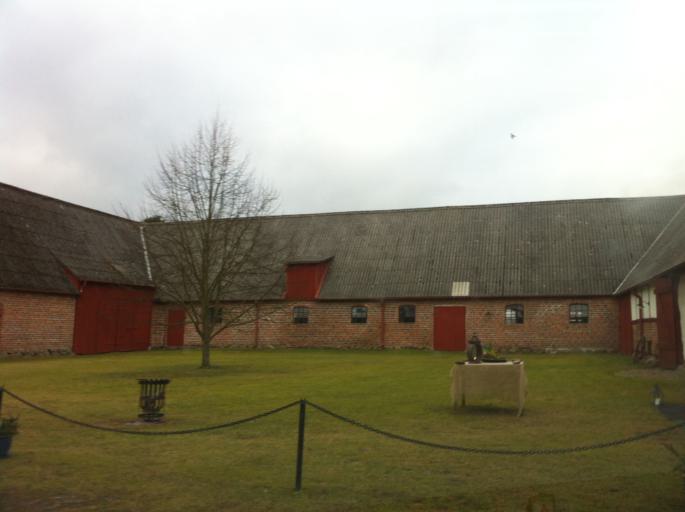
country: SE
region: Skane
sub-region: Svalovs Kommun
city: Teckomatorp
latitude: 55.8278
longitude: 13.0918
